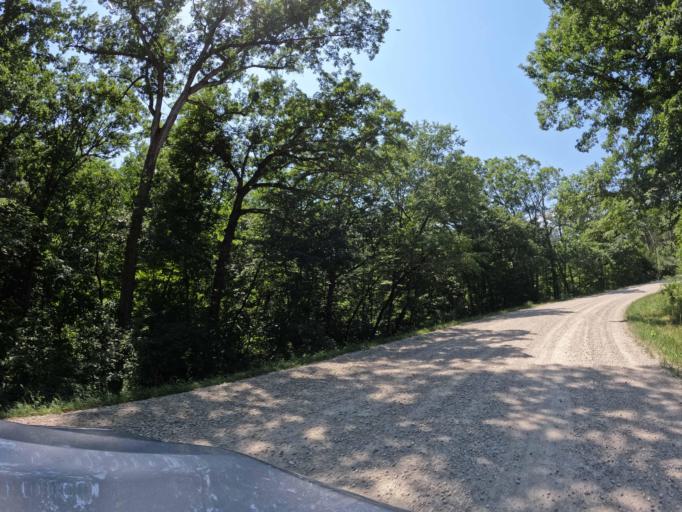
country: US
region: Iowa
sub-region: Henry County
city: Mount Pleasant
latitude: 40.8907
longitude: -91.6886
